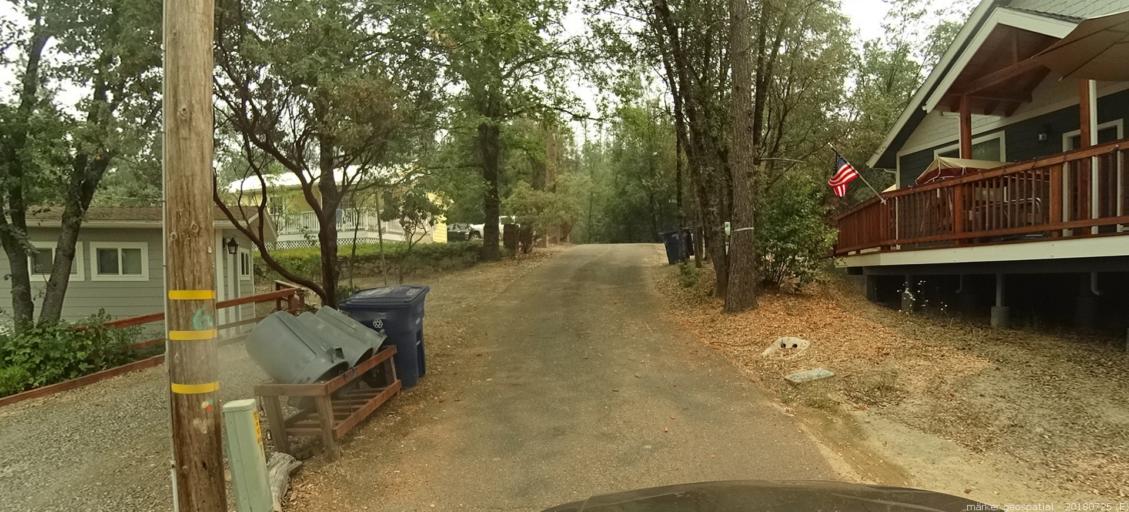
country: US
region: California
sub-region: Madera County
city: Oakhurst
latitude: 37.3230
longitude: -119.5648
